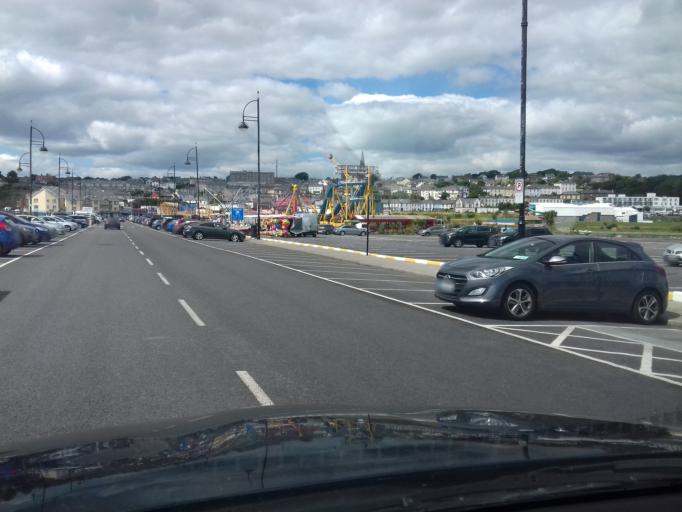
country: IE
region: Munster
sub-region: Waterford
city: Tra Mhor
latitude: 52.1594
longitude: -7.1432
